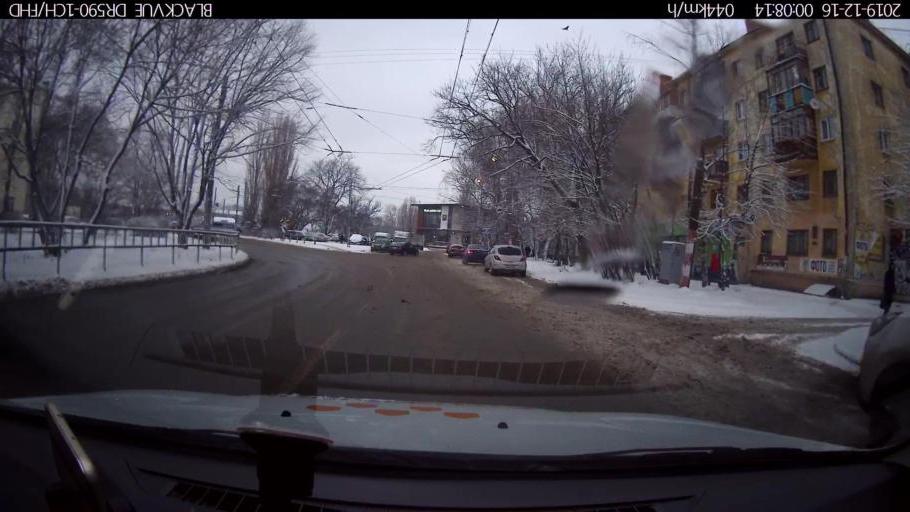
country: RU
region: Nizjnij Novgorod
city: Nizhniy Novgorod
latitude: 56.2835
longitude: 43.9289
